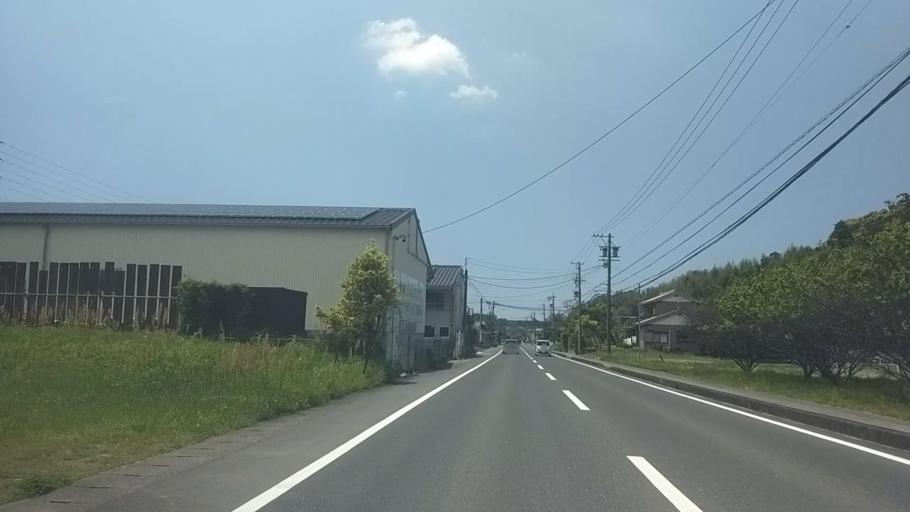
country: JP
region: Shizuoka
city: Hamamatsu
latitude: 34.7694
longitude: 137.6651
